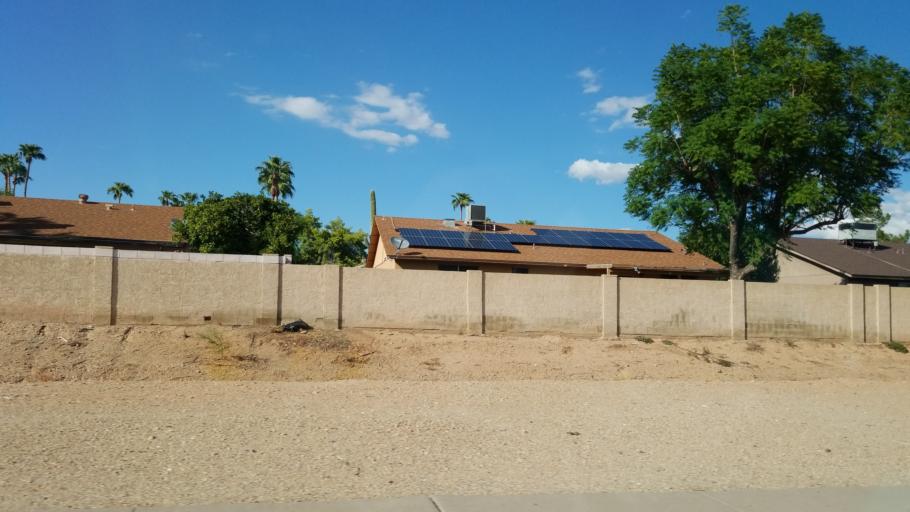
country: US
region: Arizona
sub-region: Maricopa County
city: Scottsdale
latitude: 33.5863
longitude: -111.8498
